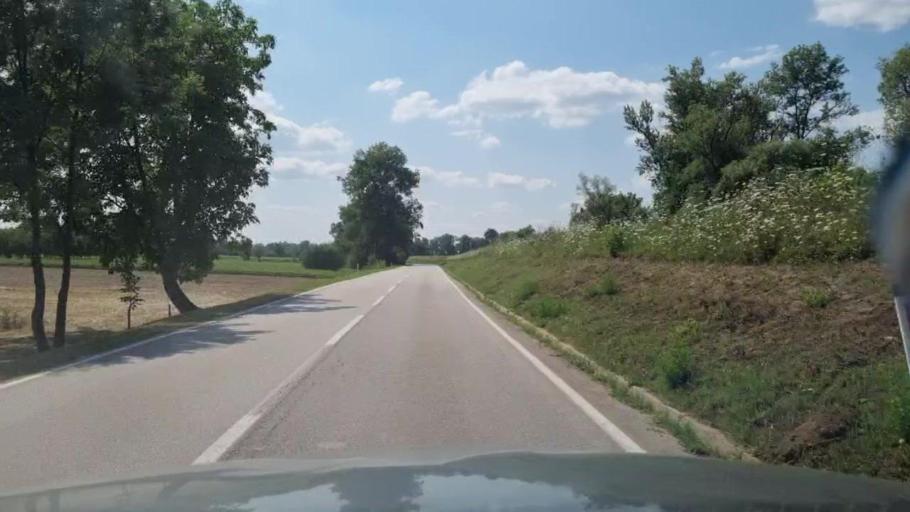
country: BA
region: Federation of Bosnia and Herzegovina
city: Donja Mahala
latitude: 45.0548
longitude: 18.6413
